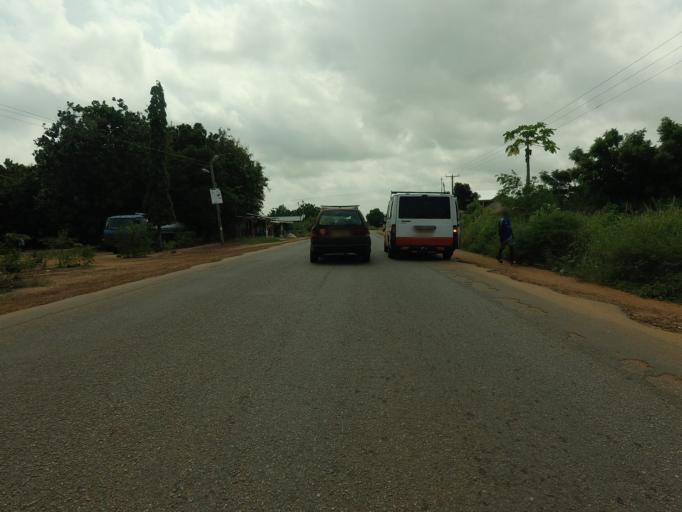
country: TG
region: Maritime
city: Lome
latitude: 6.1186
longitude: 1.1322
